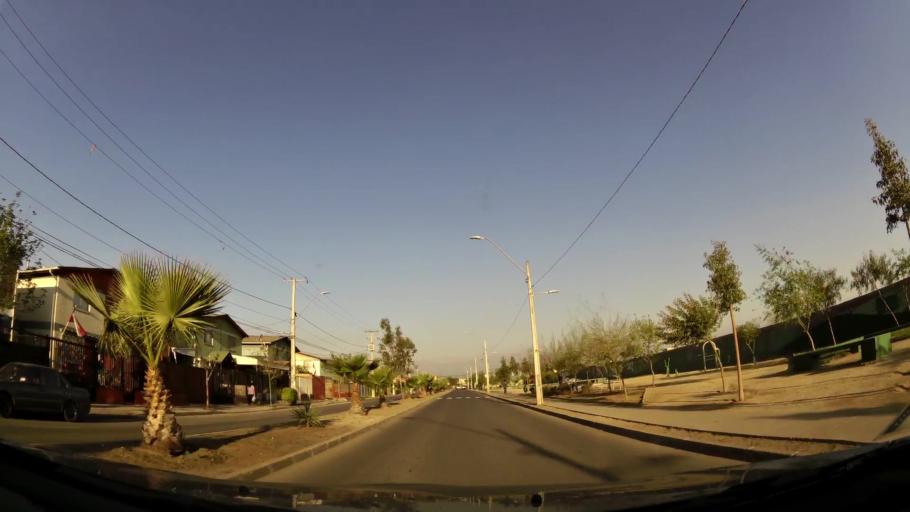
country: CL
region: Santiago Metropolitan
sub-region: Provincia de Maipo
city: San Bernardo
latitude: -33.5925
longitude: -70.6734
